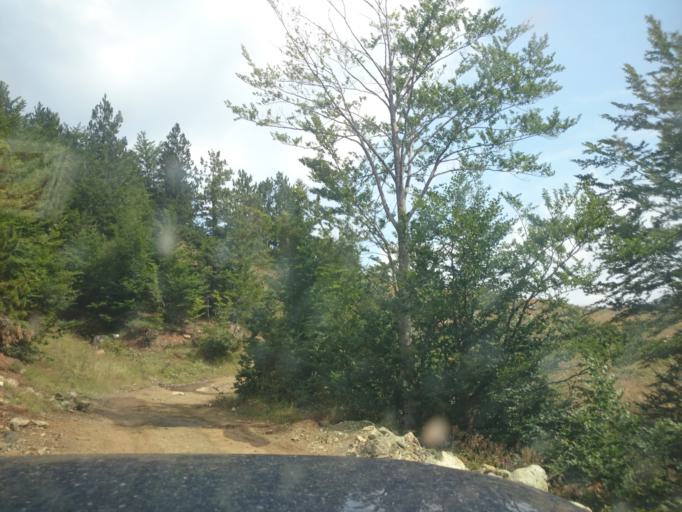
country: AL
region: Lezhe
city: Kurbnesh
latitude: 41.7870
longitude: 20.1494
